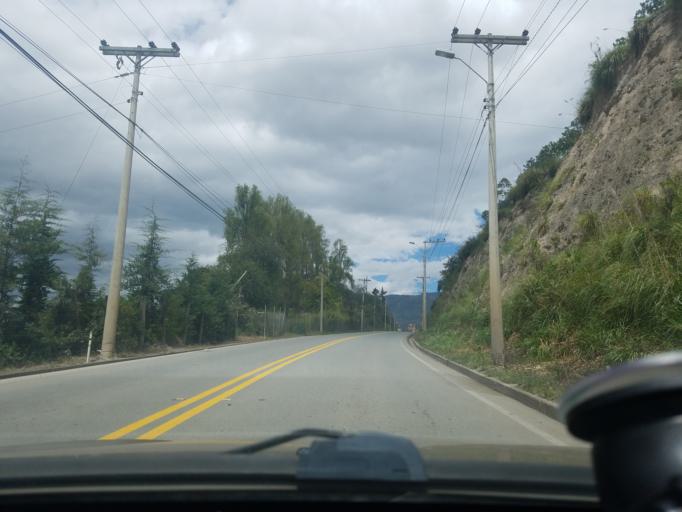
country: EC
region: Azuay
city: La Union
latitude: -2.8462
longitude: -78.7743
